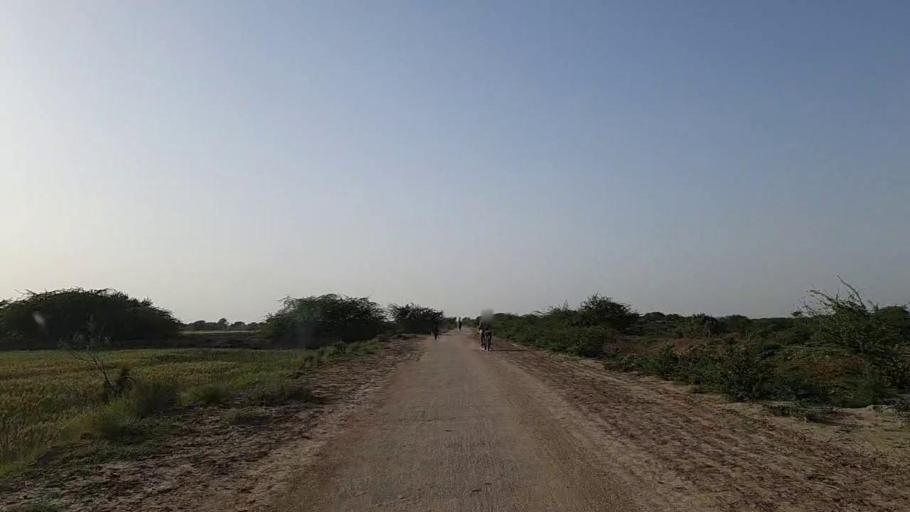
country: PK
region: Sindh
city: Jati
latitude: 24.3312
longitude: 68.1582
